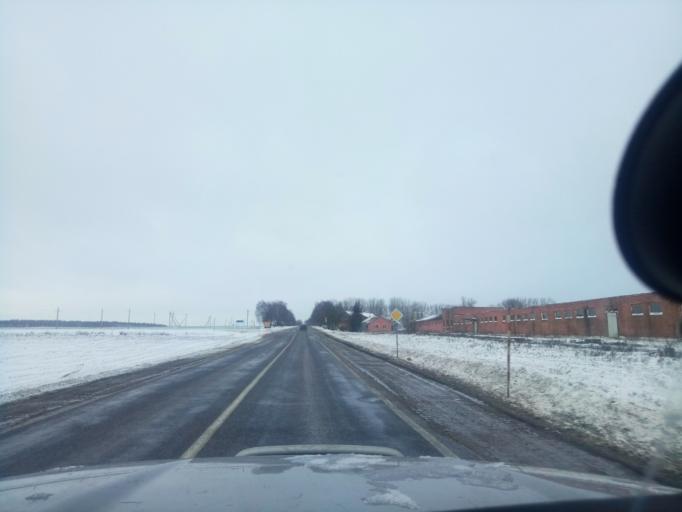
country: BY
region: Minsk
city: Tsimkavichy
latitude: 53.0849
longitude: 27.0166
